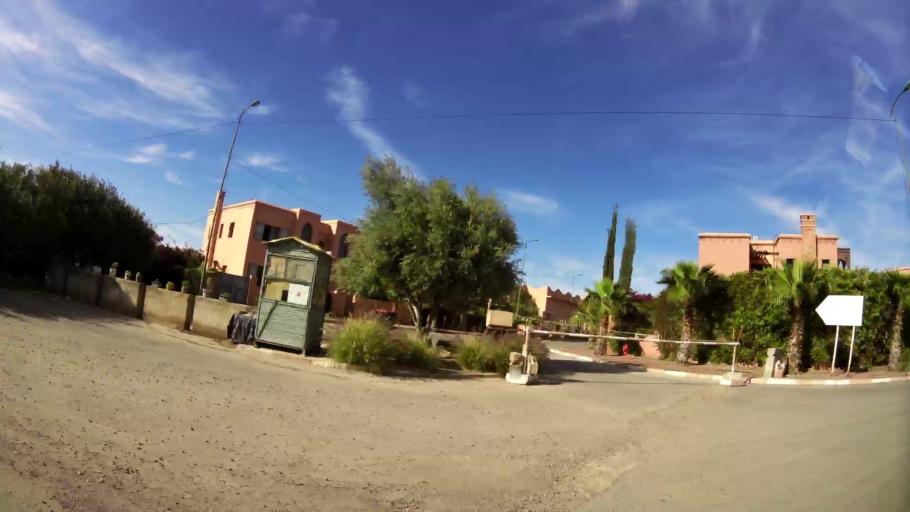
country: MA
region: Marrakech-Tensift-Al Haouz
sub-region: Marrakech
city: Marrakesh
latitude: 31.6748
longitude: -8.0559
